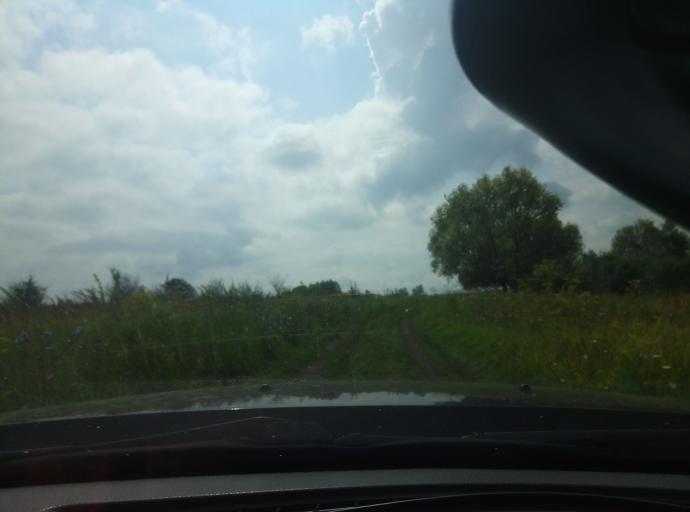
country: RU
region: Tula
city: Shvartsevskiy
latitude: 54.0831
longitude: 38.0213
